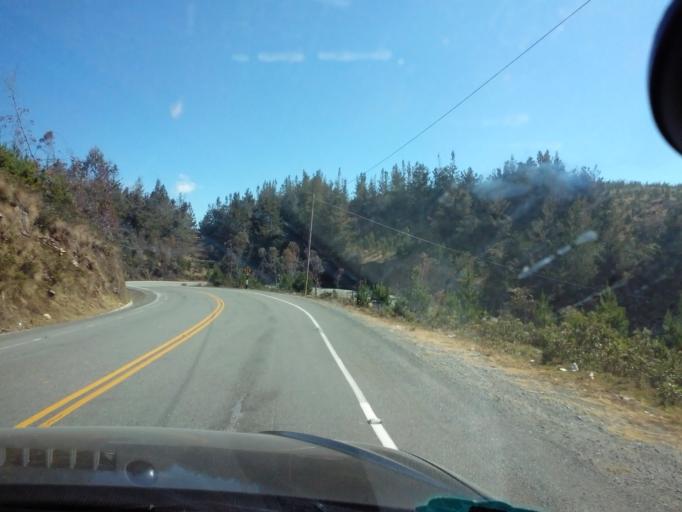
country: PE
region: Apurimac
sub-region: Provincia de Abancay
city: Cachora
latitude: -13.5572
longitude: -72.8198
